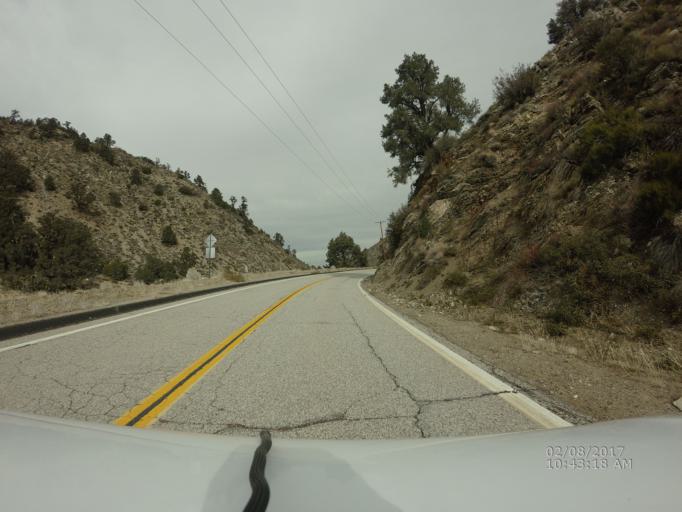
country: US
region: California
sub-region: San Bernardino County
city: Pinon Hills
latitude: 34.4254
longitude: -117.7667
